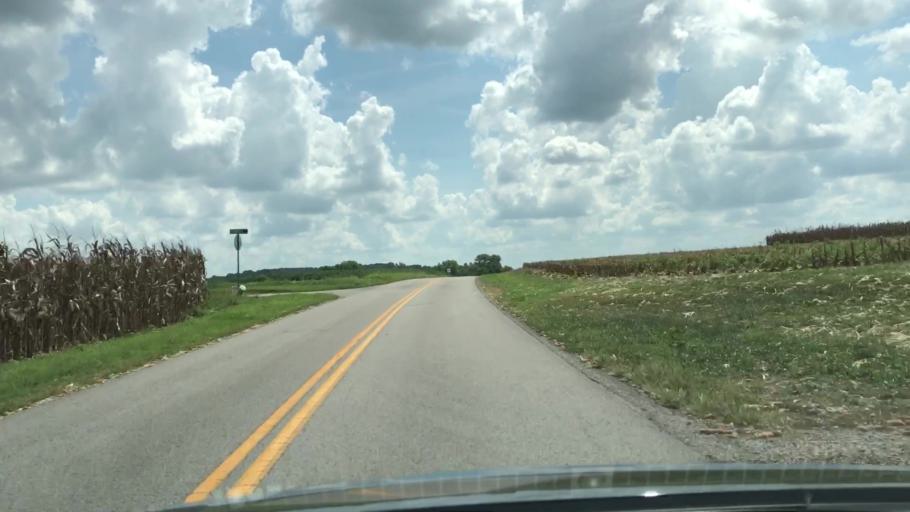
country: US
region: Kentucky
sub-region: Todd County
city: Guthrie
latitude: 36.7082
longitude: -87.0481
